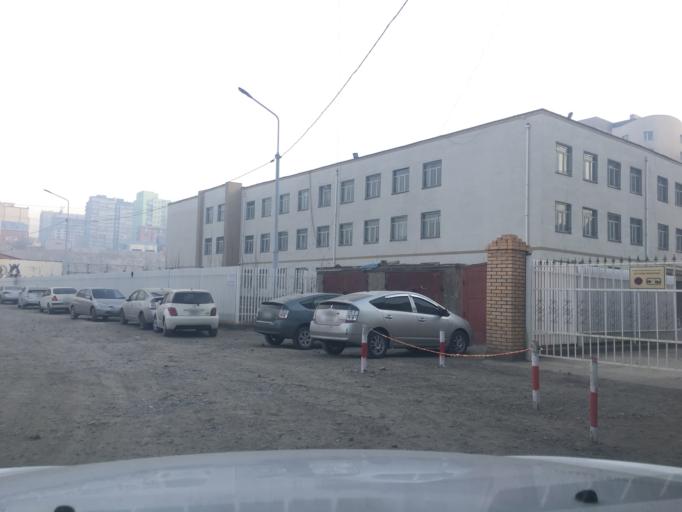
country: MN
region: Ulaanbaatar
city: Ulaanbaatar
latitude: 47.9156
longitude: 106.8655
